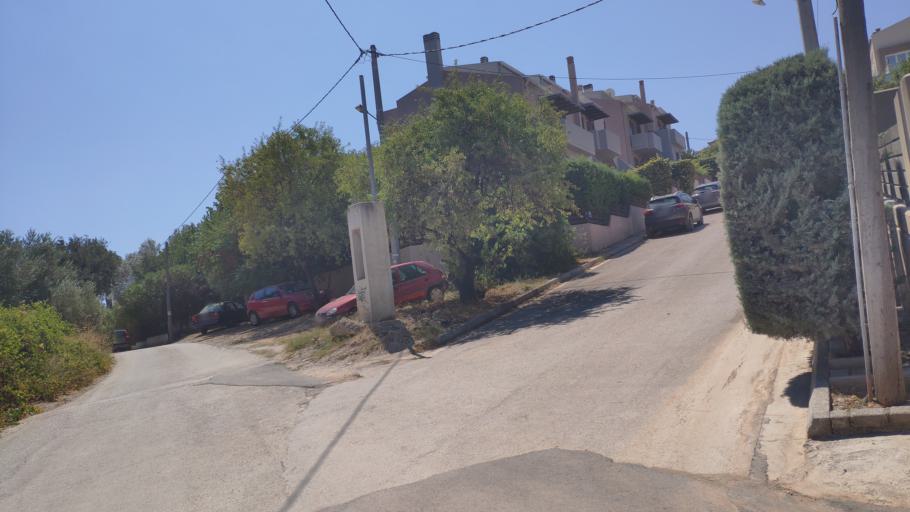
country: GR
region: Attica
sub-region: Nomarchia Anatolikis Attikis
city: Limin Mesoyaias
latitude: 37.8933
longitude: 24.0050
